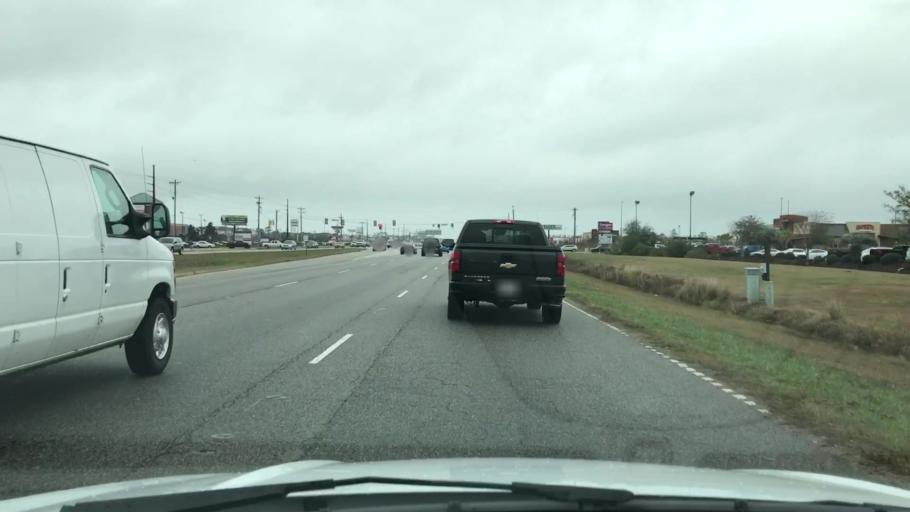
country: US
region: South Carolina
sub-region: Horry County
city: Forestbrook
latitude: 33.7511
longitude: -78.9610
